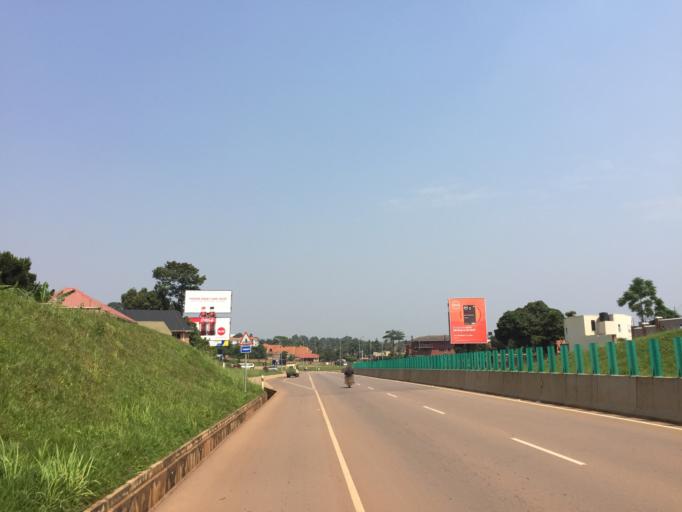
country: UG
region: Central Region
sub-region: Kampala District
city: Kampala
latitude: 0.2390
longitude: 32.6190
